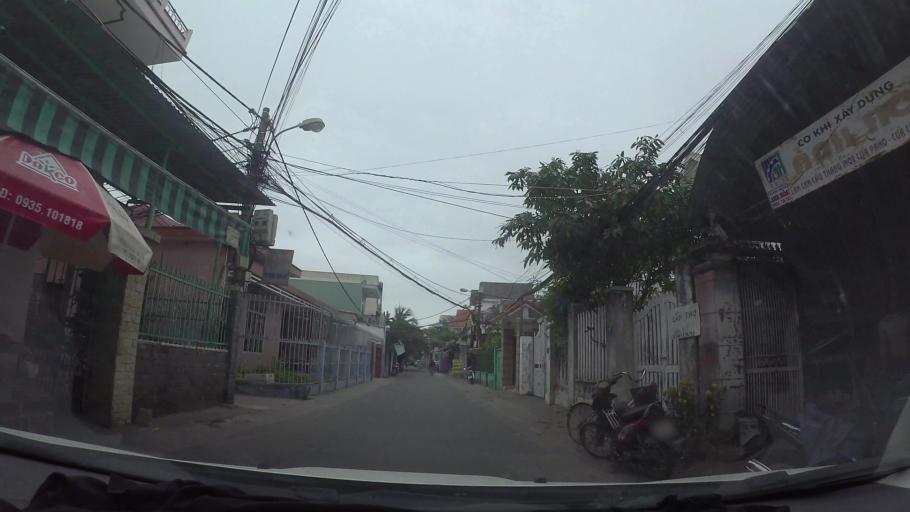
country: VN
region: Da Nang
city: Lien Chieu
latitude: 16.0722
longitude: 108.1468
